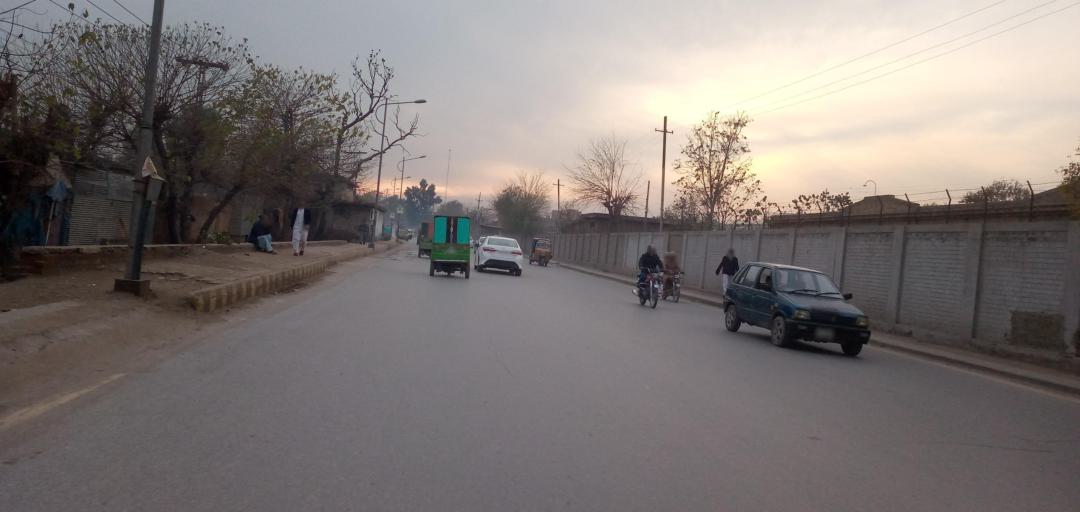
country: PK
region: Khyber Pakhtunkhwa
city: Peshawar
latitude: 34.0010
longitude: 71.5510
